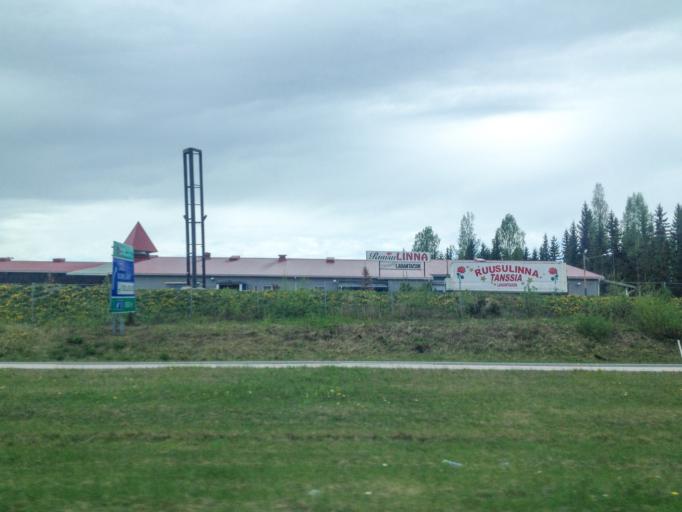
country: FI
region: Uusimaa
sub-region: Helsinki
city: Nurmijaervi
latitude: 60.4737
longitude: 24.8497
